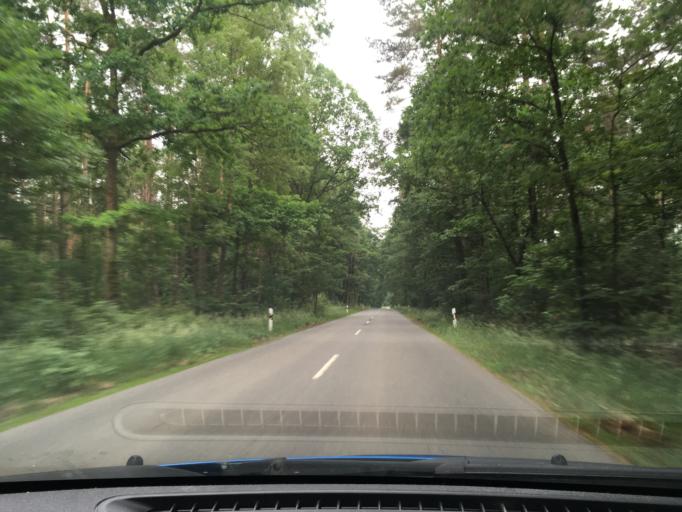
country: DE
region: Lower Saxony
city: Zernien
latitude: 53.0821
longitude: 10.8836
